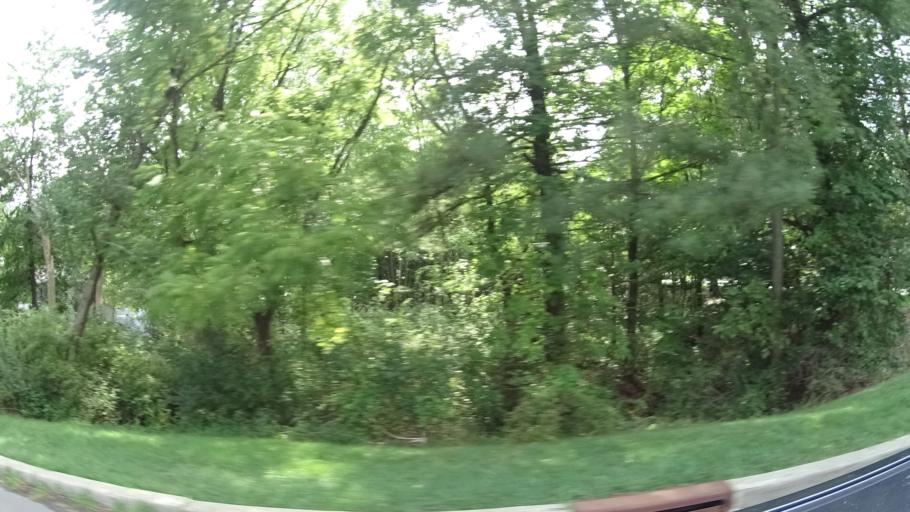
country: US
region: New Jersey
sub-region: Somerset County
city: Warren Township
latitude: 40.6592
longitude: -74.5312
